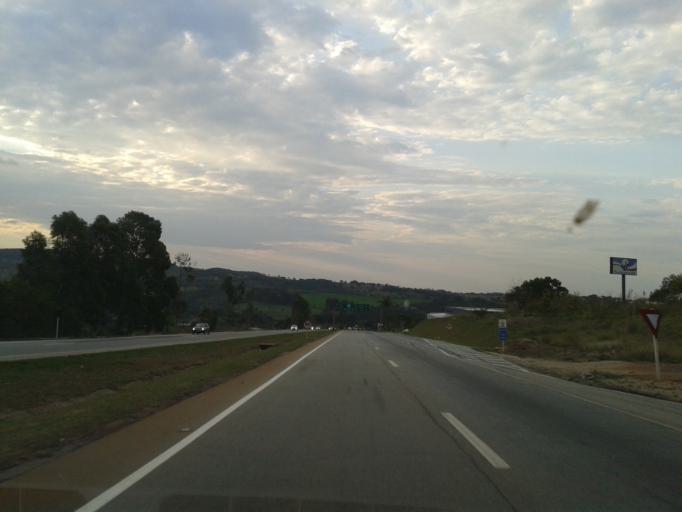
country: BR
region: Minas Gerais
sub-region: Juatuba
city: Juatuba
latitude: -19.9363
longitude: -44.3913
